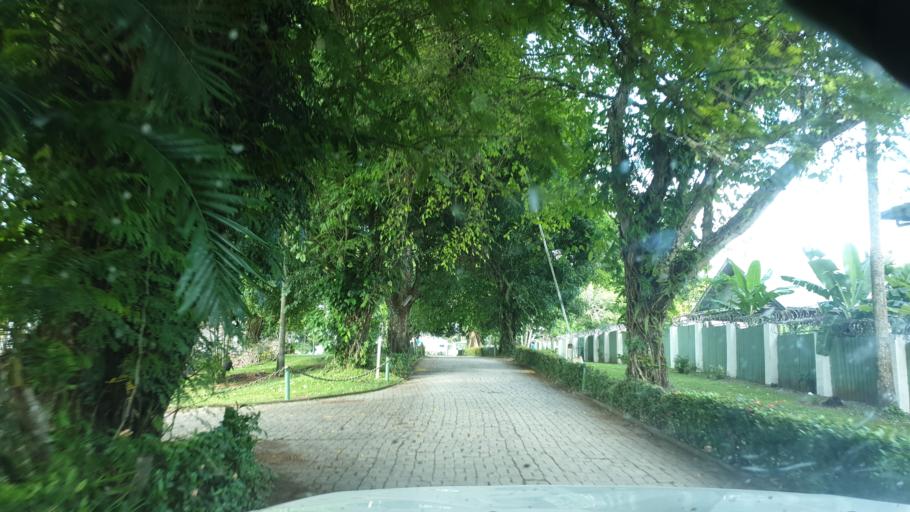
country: PG
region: Madang
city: Madang
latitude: -5.2089
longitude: 145.8090
